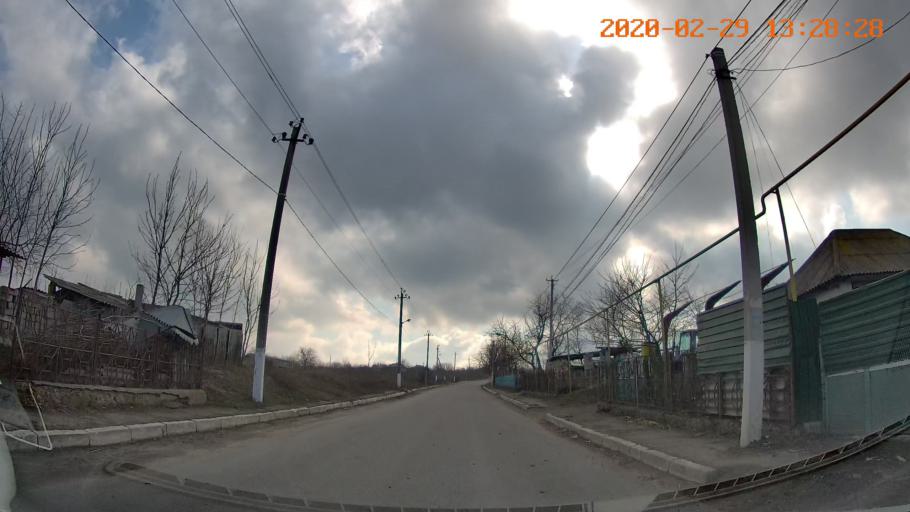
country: MD
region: Telenesti
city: Camenca
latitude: 47.9051
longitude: 28.6423
